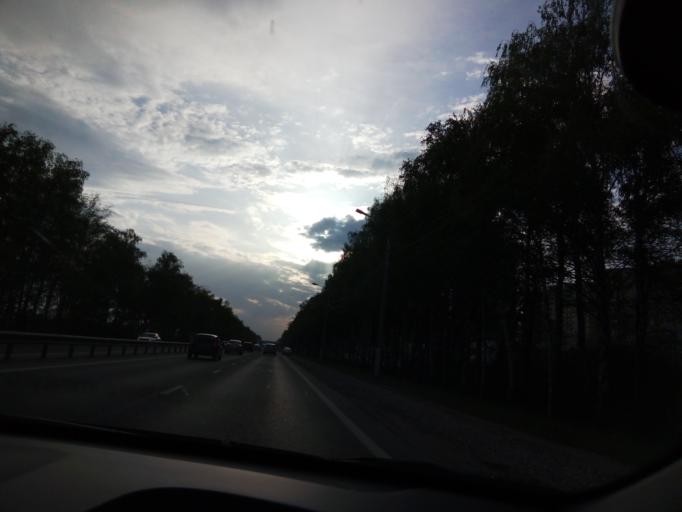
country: RU
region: Chuvashia
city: Novocheboksarsk
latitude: 56.1241
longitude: 47.3940
